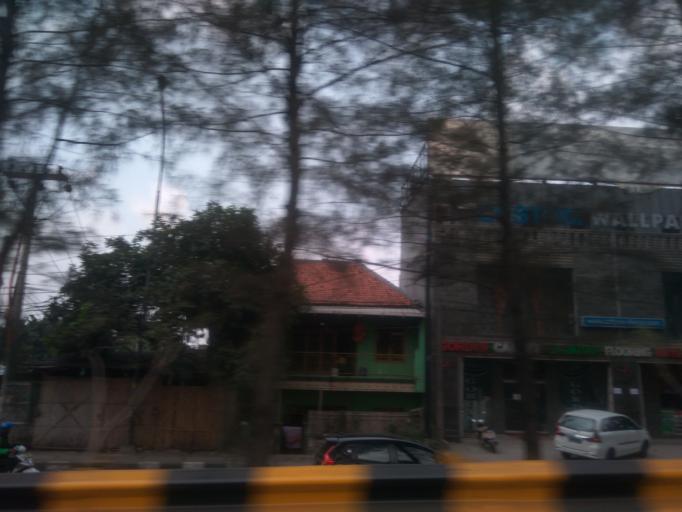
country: ID
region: West Java
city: Bekasi
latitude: -6.2517
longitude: 106.9916
